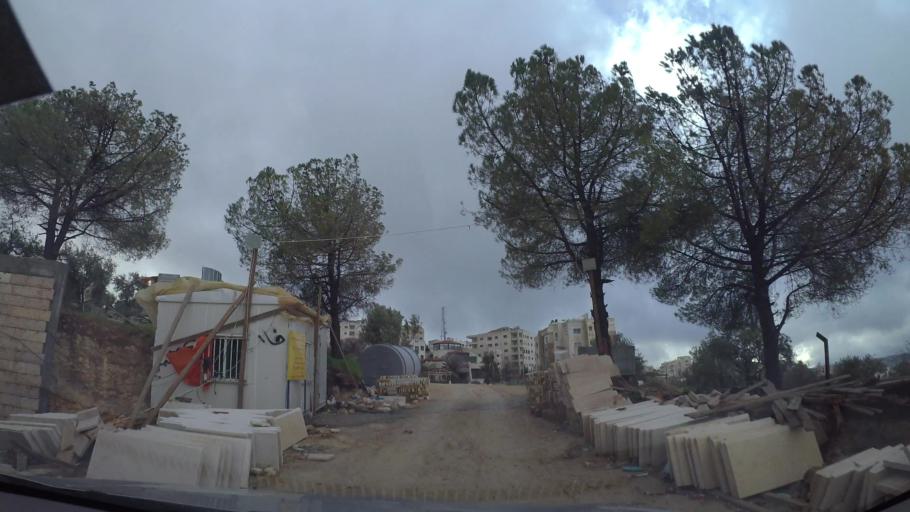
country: JO
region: Amman
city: Al Jubayhah
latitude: 32.0328
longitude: 35.8543
